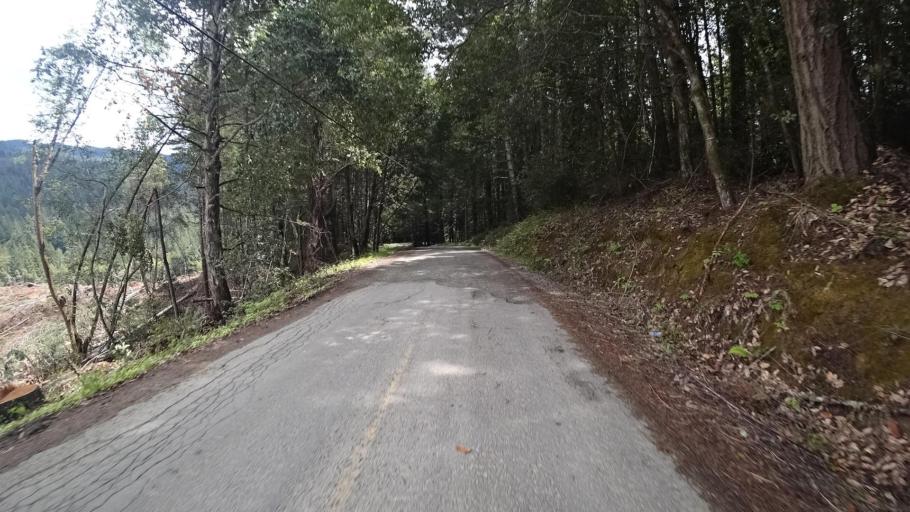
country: US
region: California
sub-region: Humboldt County
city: Blue Lake
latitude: 40.8005
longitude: -123.8769
